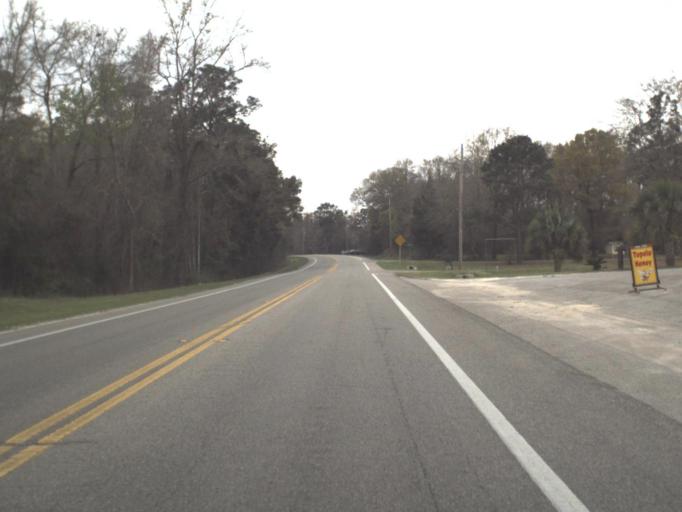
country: US
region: Florida
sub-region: Gulf County
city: Wewahitchka
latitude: 30.1462
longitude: -85.2098
